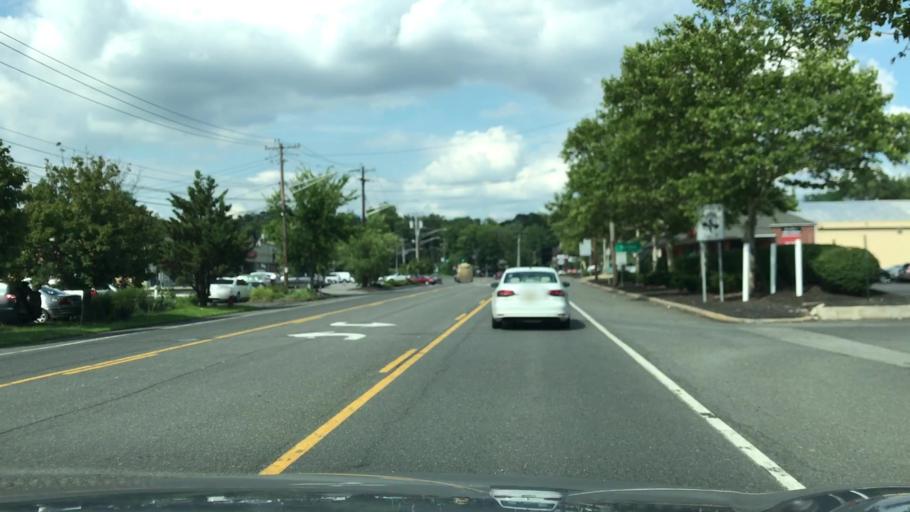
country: US
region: New York
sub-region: Rockland County
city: Tappan
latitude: 41.0172
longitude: -73.9443
